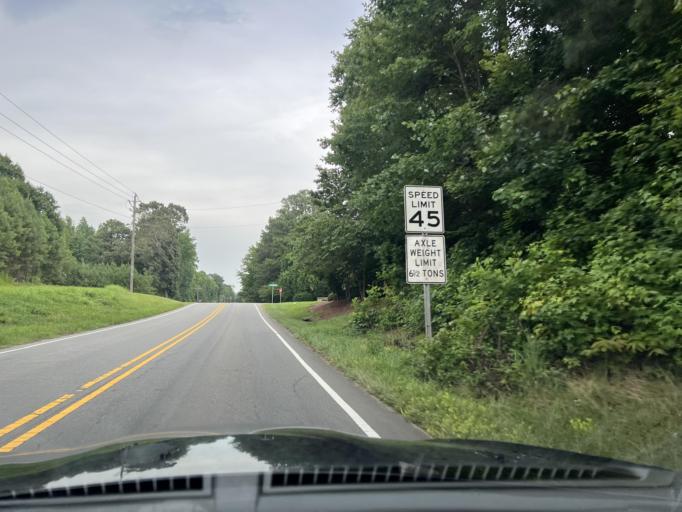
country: US
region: North Carolina
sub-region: Wake County
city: Wake Forest
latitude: 36.0153
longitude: -78.5719
